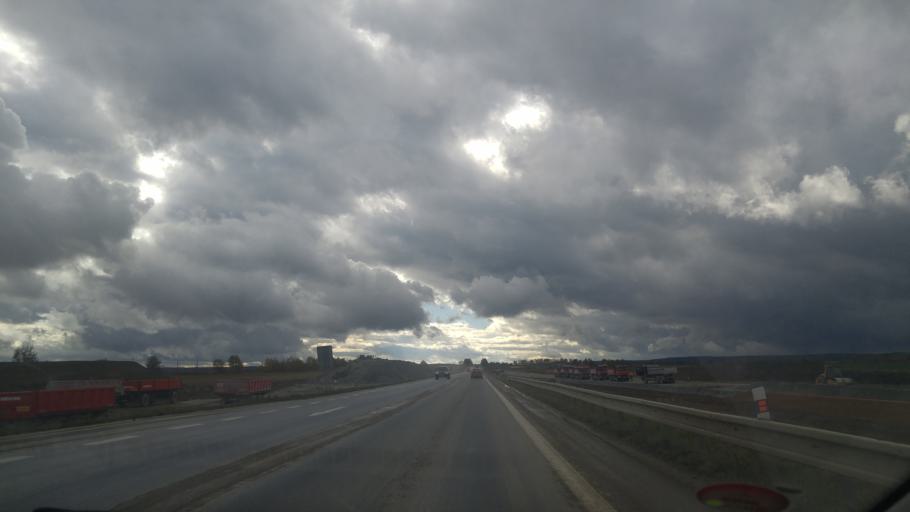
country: CZ
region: Jihocesky
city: Dolni Bukovsko
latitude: 49.1417
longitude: 14.6202
